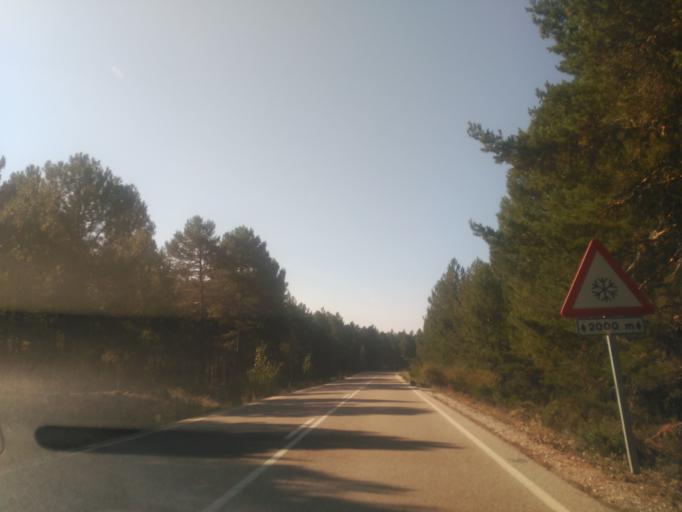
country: ES
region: Castille and Leon
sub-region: Provincia de Soria
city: Herrera de Soria
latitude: 41.7621
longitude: -3.0339
